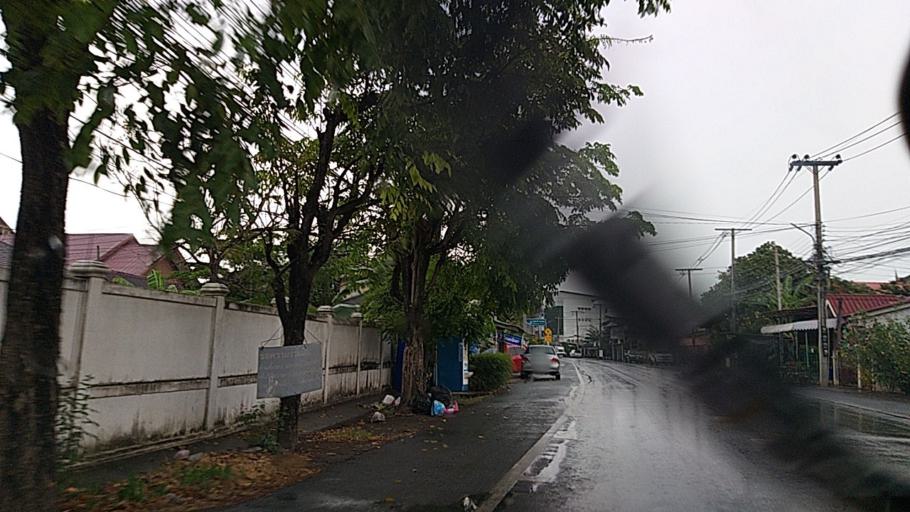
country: TH
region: Phra Nakhon Si Ayutthaya
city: Phra Nakhon Si Ayutthaya
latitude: 14.3584
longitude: 100.5503
